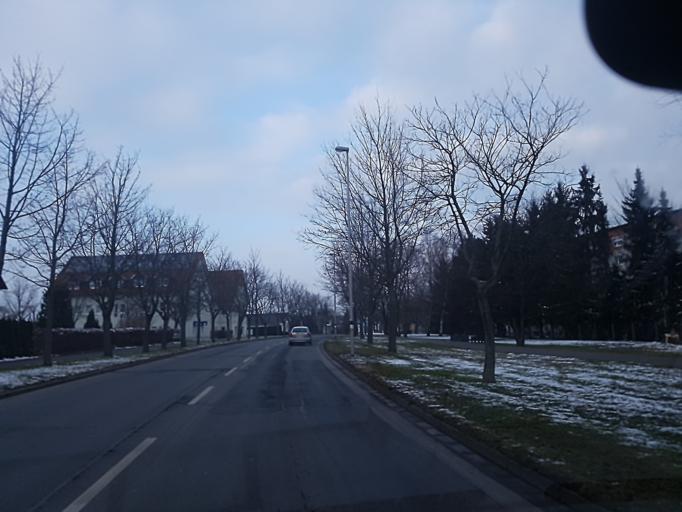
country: DE
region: Saxony
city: Oschatz
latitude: 51.3004
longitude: 13.0955
